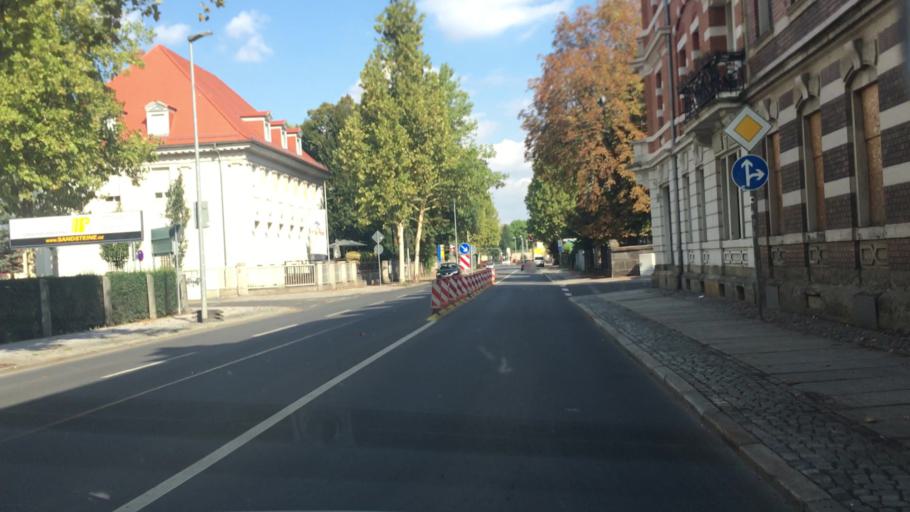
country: DE
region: Saxony
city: Pirna
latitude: 50.9591
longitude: 13.9311
